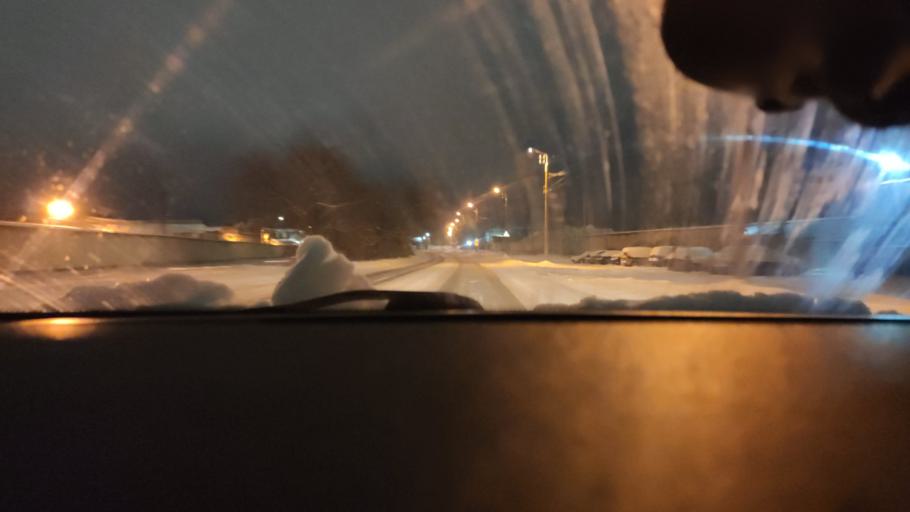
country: RU
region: Perm
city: Krasnokamsk
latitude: 58.0791
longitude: 55.7741
